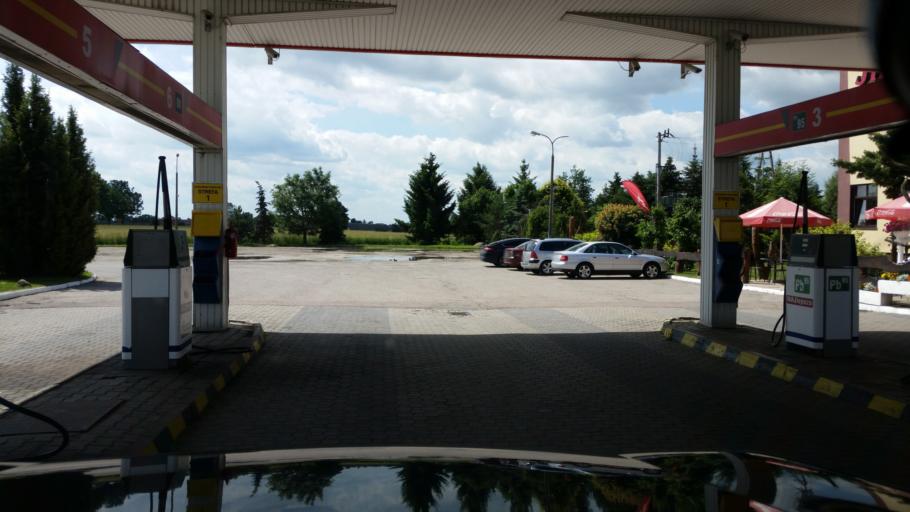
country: PL
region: Podlasie
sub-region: Powiat lomzynski
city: Piatnica
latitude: 53.2588
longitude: 22.1230
